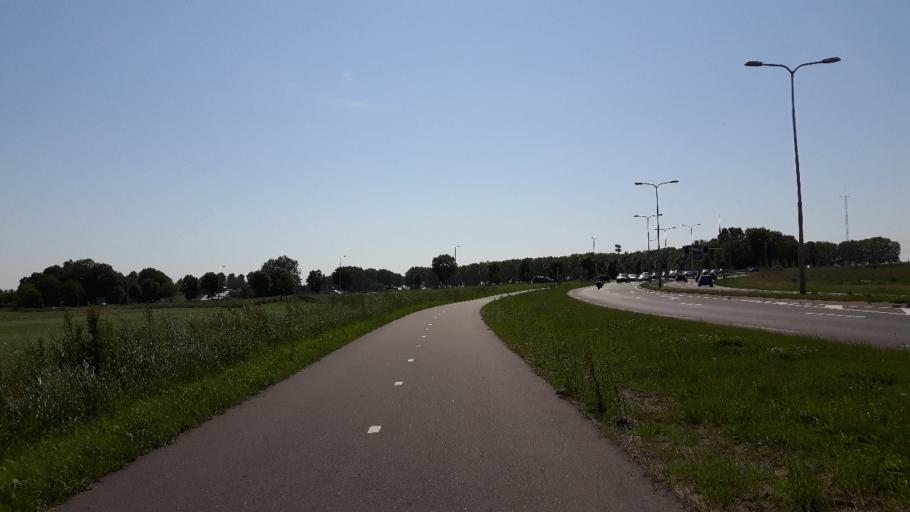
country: NL
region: Utrecht
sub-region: Stichtse Vecht
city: Vreeland
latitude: 52.2249
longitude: 5.0152
